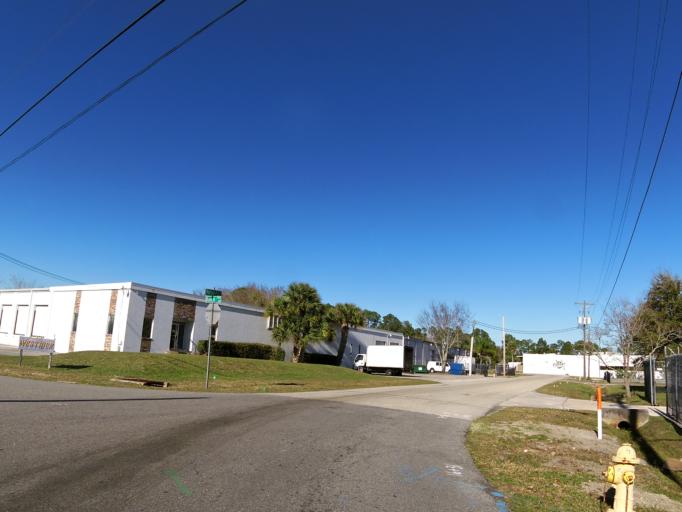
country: US
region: Florida
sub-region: Duval County
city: Jacksonville
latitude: 30.2690
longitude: -81.6261
